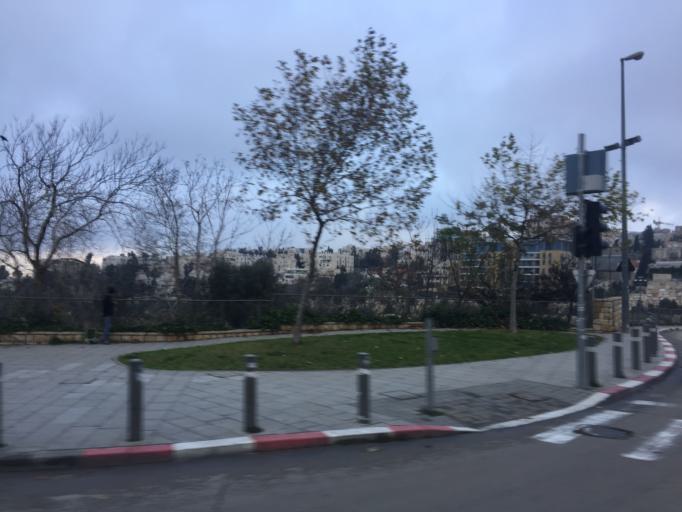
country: IL
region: Jerusalem
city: West Jerusalem
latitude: 31.7912
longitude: 35.1969
